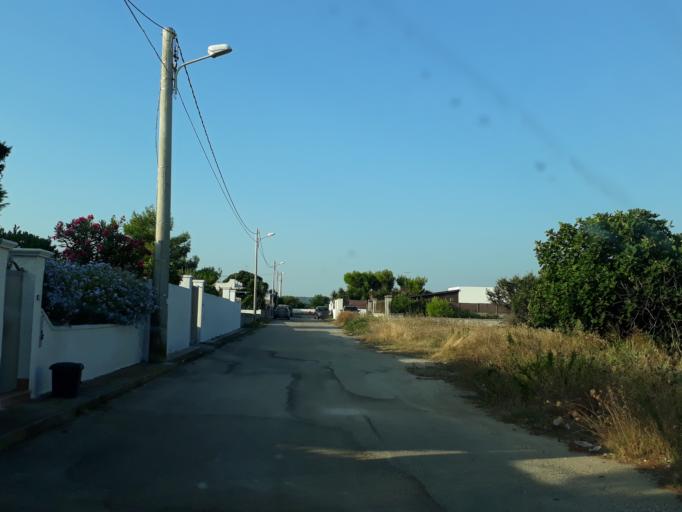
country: IT
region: Apulia
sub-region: Provincia di Brindisi
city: Carovigno
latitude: 40.7543
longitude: 17.7050
